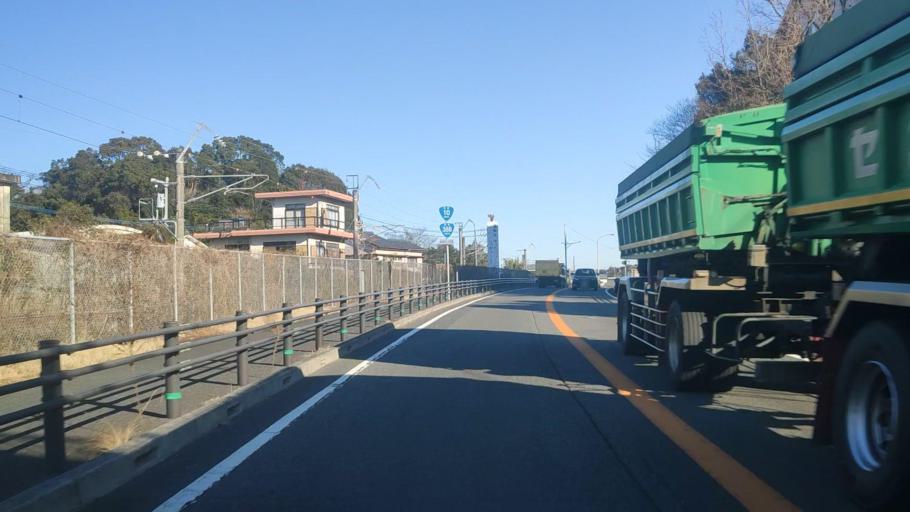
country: JP
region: Miyazaki
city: Nobeoka
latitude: 32.5175
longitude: 131.6823
